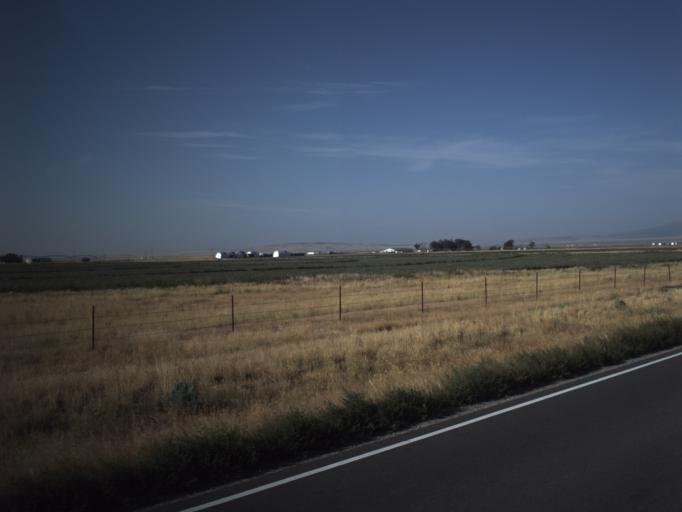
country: US
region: Idaho
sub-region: Oneida County
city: Malad City
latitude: 41.9674
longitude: -112.8256
